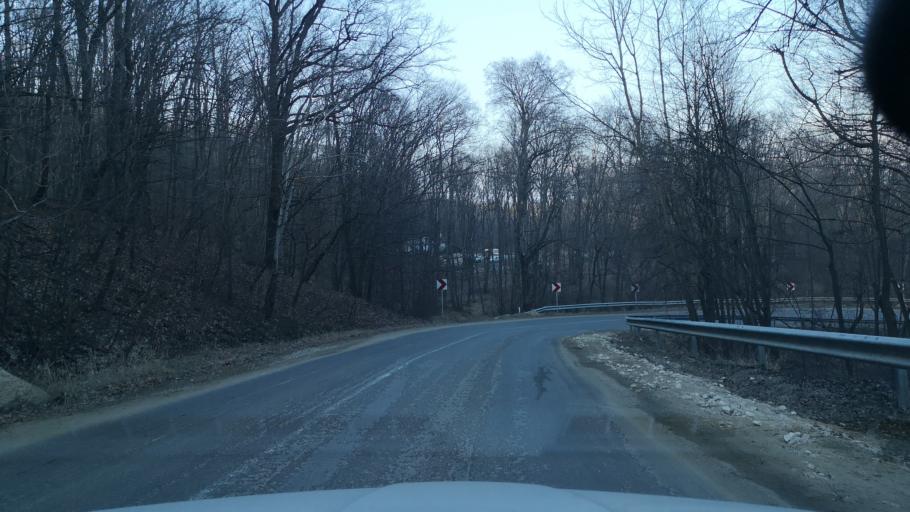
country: MD
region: Stinga Nistrului
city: Bucovat
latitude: 47.1391
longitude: 28.4961
